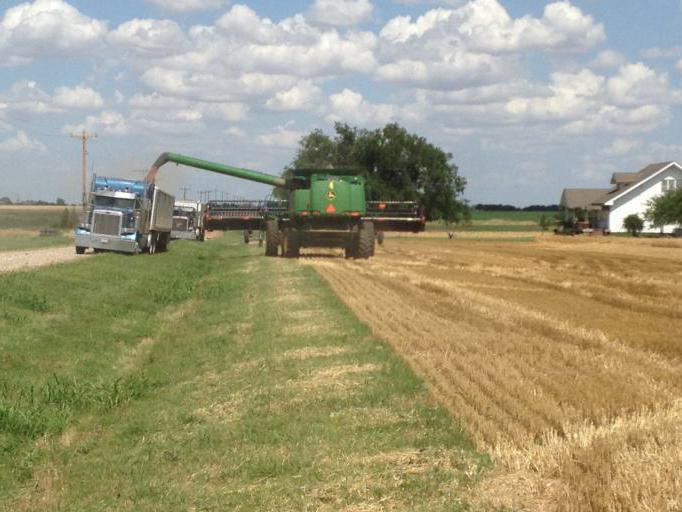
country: US
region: Oklahoma
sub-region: Alfalfa County
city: Helena
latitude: 36.6515
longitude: -98.0437
